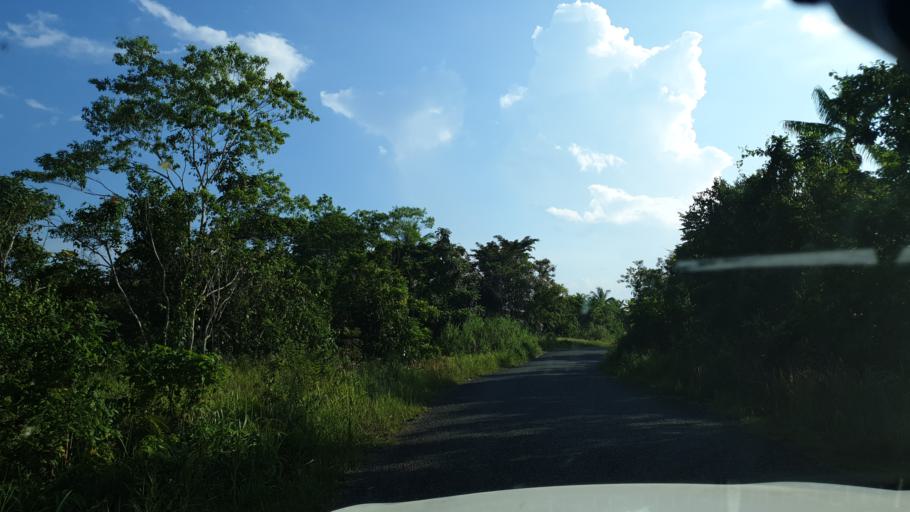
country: PG
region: East Sepik
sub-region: Wewak
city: Wewak
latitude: -3.6989
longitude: 143.6455
